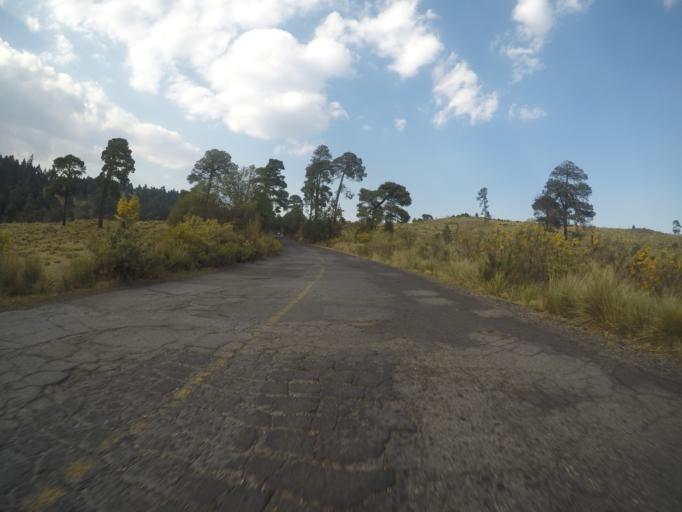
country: MX
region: Mexico
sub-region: Xalatlaco
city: San Juan Tomasquillo Herradura
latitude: 19.1851
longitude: -99.3525
